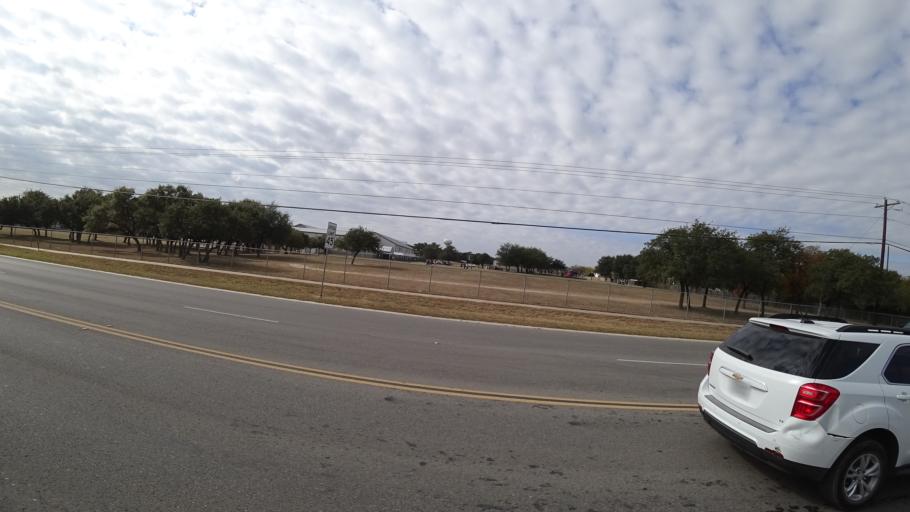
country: US
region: Texas
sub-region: Williamson County
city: Cedar Park
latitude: 30.5251
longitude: -97.8430
